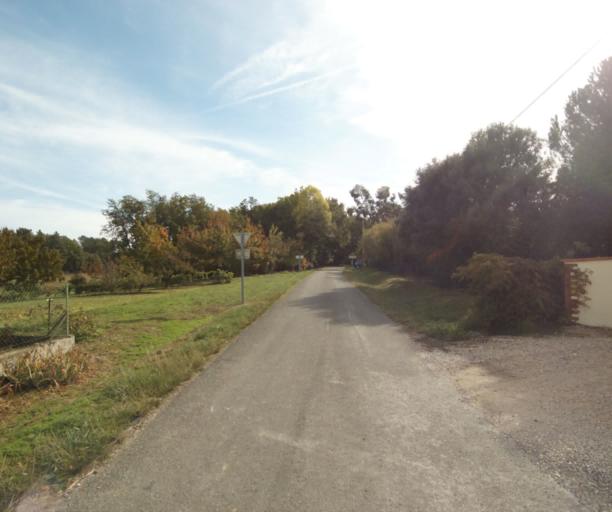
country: FR
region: Midi-Pyrenees
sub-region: Departement du Tarn-et-Garonne
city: Orgueil
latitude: 43.8962
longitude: 1.4100
